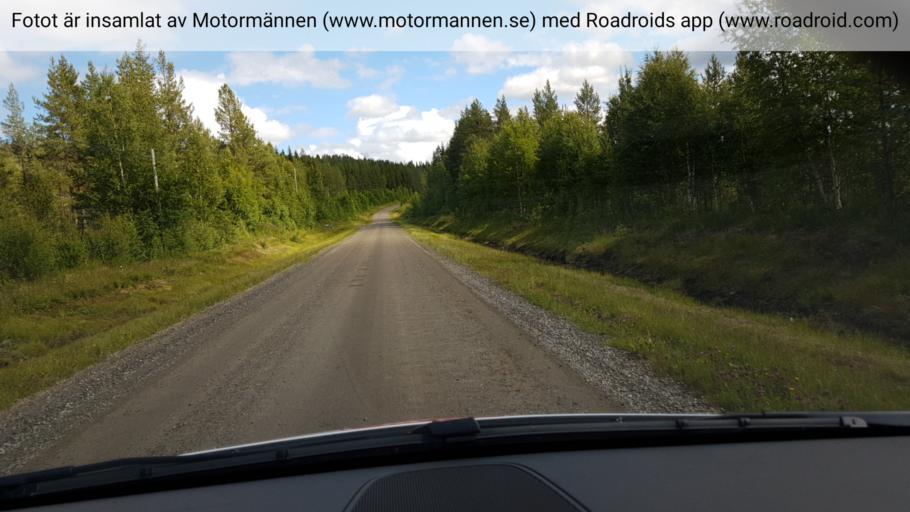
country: SE
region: Vaesterbotten
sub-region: Dorotea Kommun
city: Dorotea
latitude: 64.0900
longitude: 16.5244
